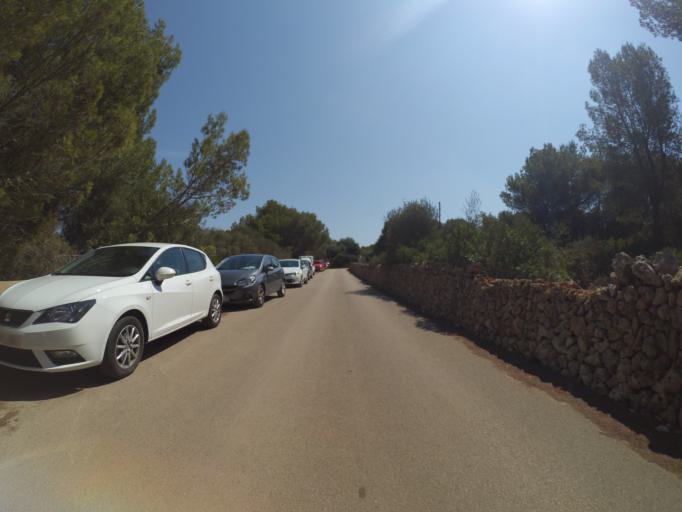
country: ES
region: Balearic Islands
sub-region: Illes Balears
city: Santanyi
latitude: 39.3930
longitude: 3.2457
